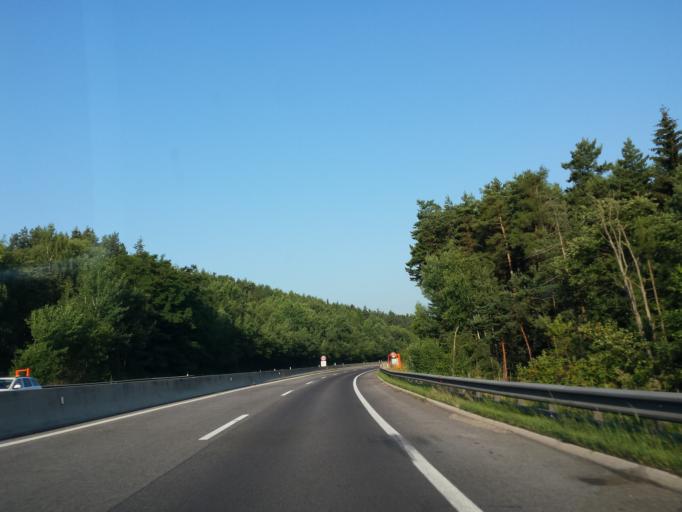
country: AT
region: Lower Austria
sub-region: Politischer Bezirk Neunkirchen
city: Wimpassing im Schwarzatale
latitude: 47.6796
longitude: 16.0280
